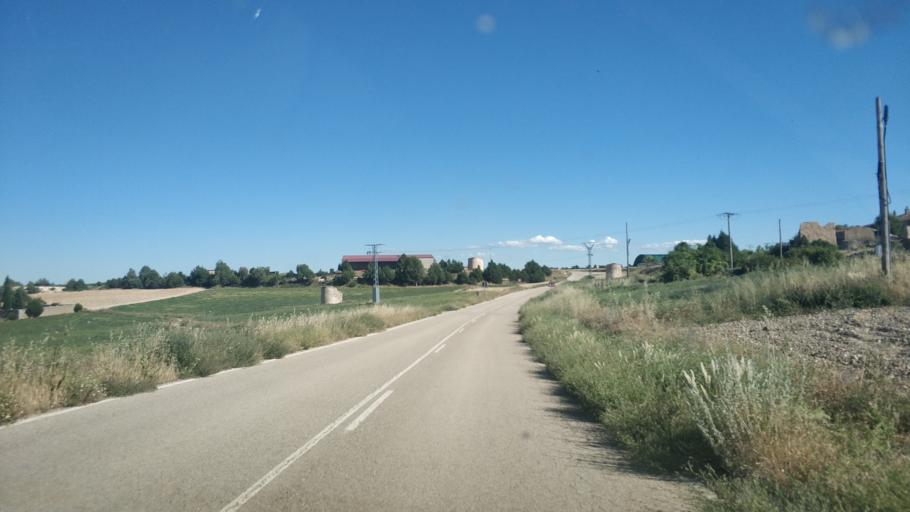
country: ES
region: Castille and Leon
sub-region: Provincia de Soria
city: Liceras
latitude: 41.4649
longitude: -3.2151
